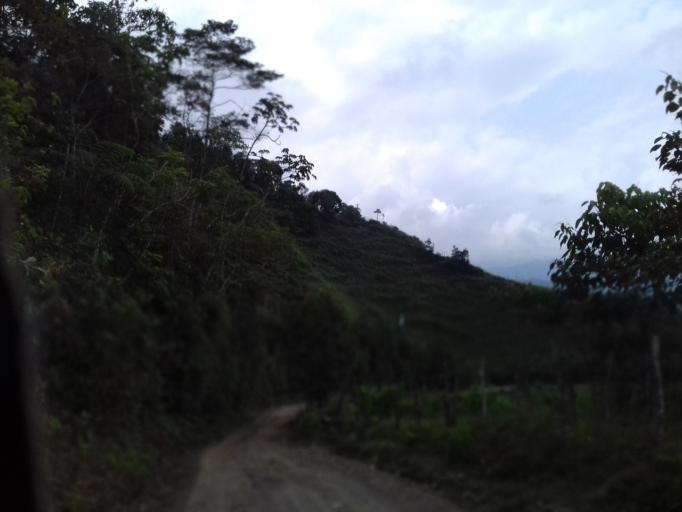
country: CO
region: Tolima
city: Libano
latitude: 4.9404
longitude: -75.0602
